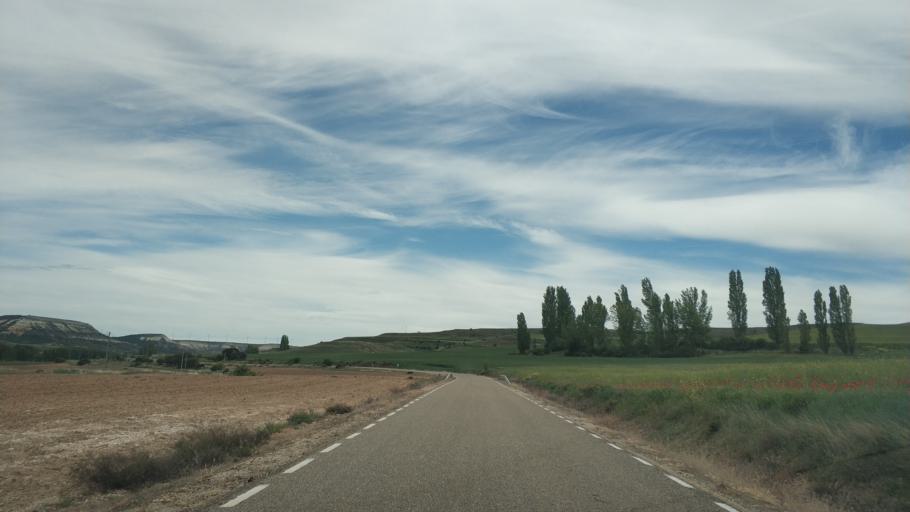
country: ES
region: Castille and Leon
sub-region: Provincia de Soria
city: Berlanga de Duero
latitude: 41.4368
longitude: -2.8139
